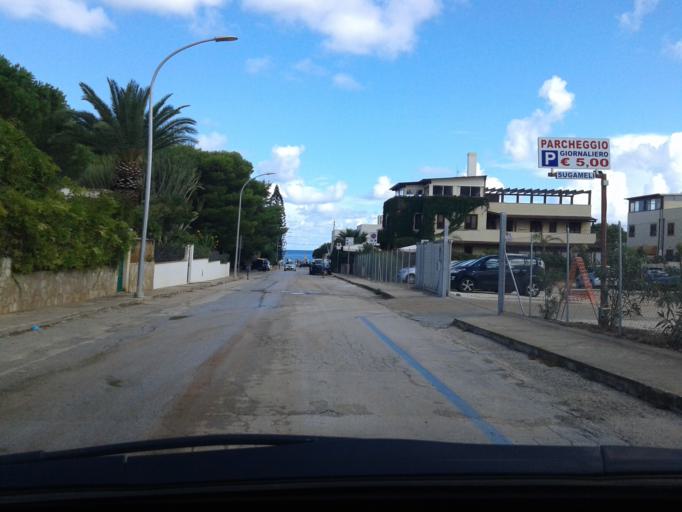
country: IT
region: Sicily
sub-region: Trapani
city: San Vito Lo Capo
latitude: 38.1733
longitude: 12.7423
